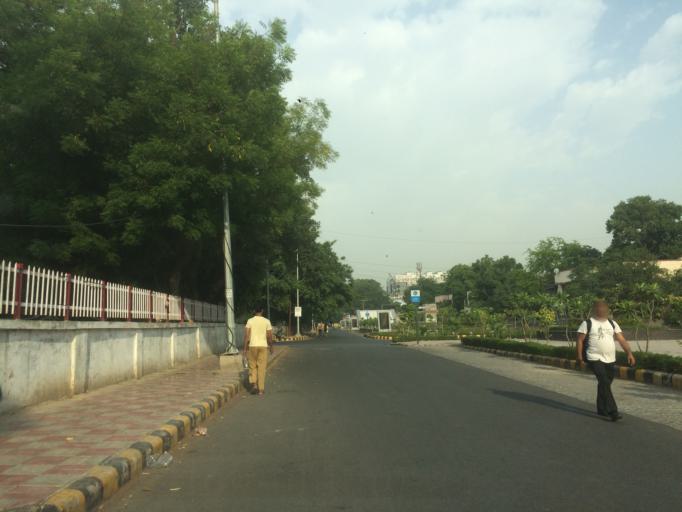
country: IN
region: NCT
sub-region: New Delhi
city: New Delhi
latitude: 28.5757
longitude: 77.1995
